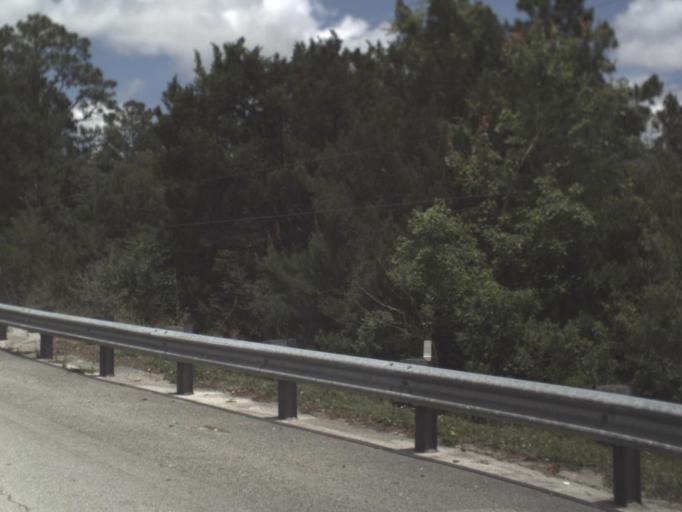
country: US
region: Florida
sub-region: Nassau County
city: Yulee
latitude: 30.5918
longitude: -81.5996
